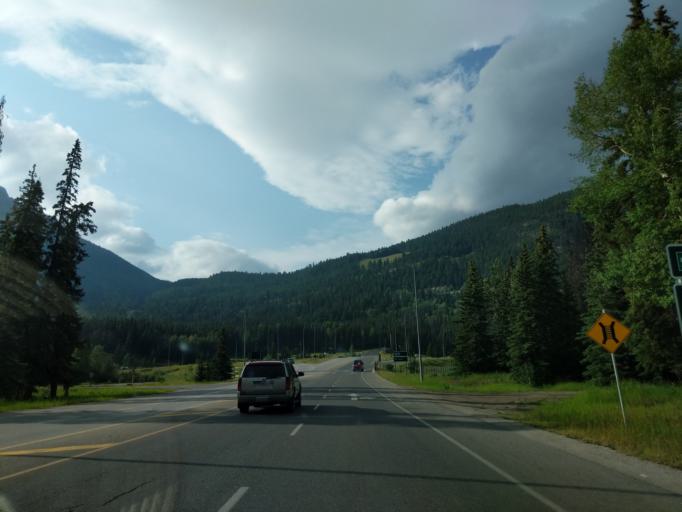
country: CA
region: Alberta
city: Banff
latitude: 51.1854
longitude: -115.5818
